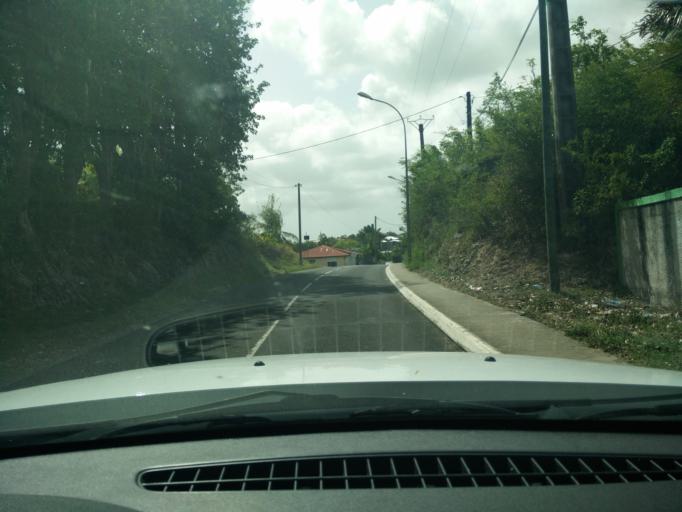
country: GP
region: Guadeloupe
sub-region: Guadeloupe
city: Le Gosier
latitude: 16.2165
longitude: -61.4521
